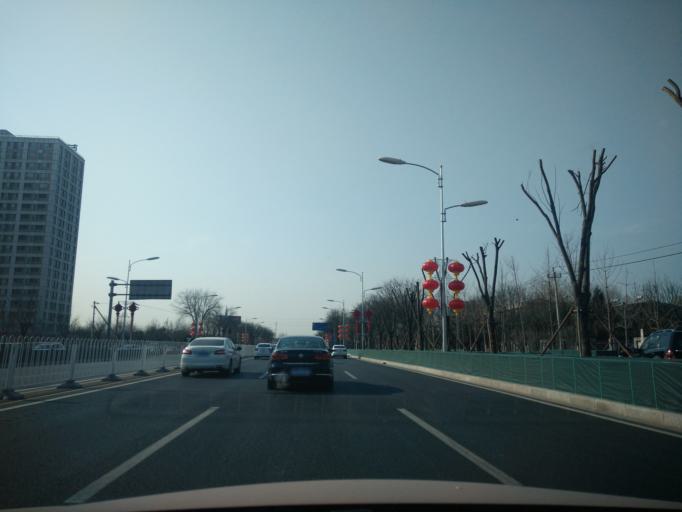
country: CN
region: Beijing
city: Jiugong
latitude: 39.7850
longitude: 116.4899
